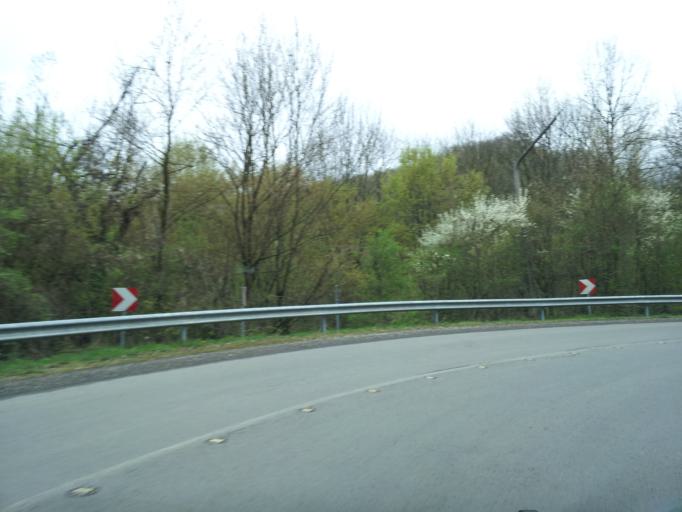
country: HU
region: Borsod-Abauj-Zemplen
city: Rudabanya
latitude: 48.4811
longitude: 20.5458
